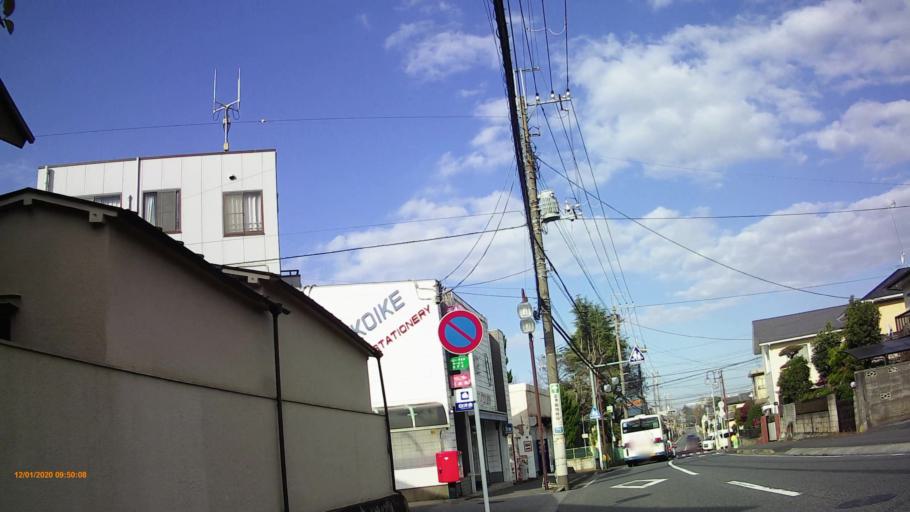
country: JP
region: Chiba
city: Yotsukaido
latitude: 35.6224
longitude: 140.1930
